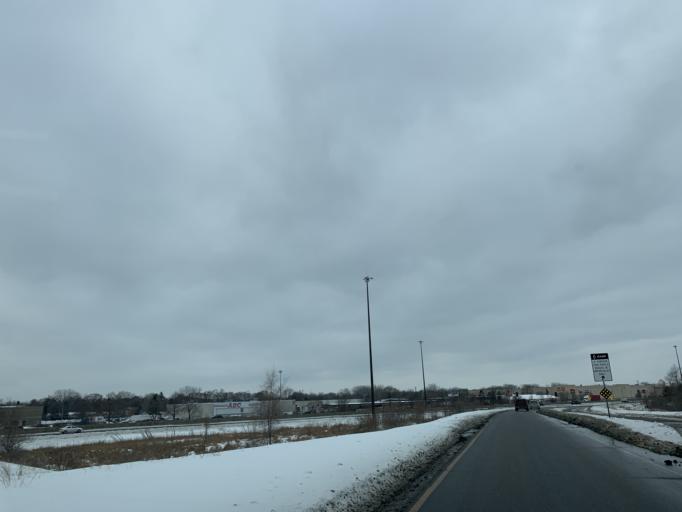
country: US
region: Minnesota
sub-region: Anoka County
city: Coon Rapids
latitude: 45.1543
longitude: -93.2744
